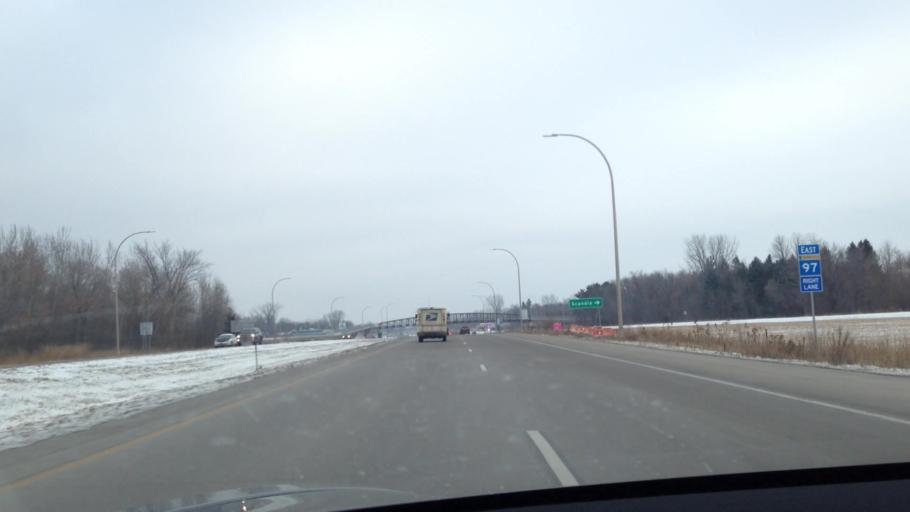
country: US
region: Minnesota
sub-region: Washington County
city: Forest Lake
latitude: 45.2562
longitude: -92.9838
